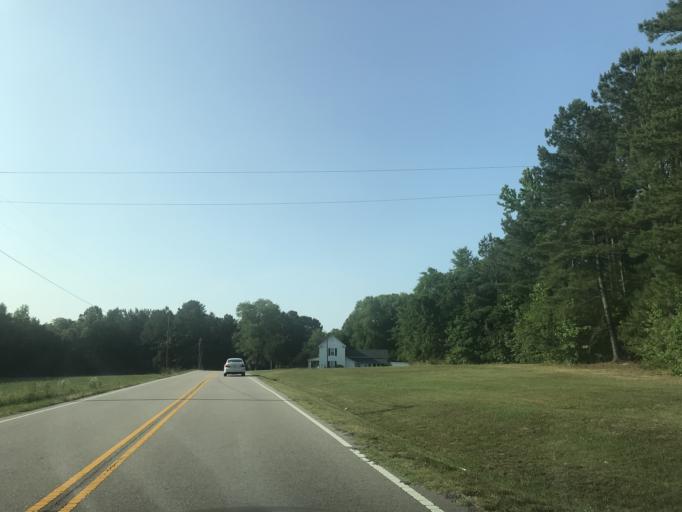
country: US
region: North Carolina
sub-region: Wake County
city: Knightdale
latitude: 35.8419
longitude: -78.5013
